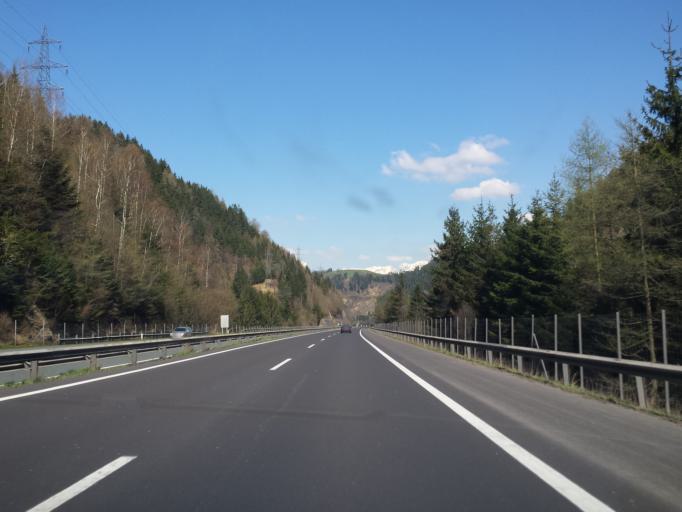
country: AT
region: Styria
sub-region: Politischer Bezirk Leoben
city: Sankt Michael in Obersteiermark
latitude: 47.3059
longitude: 15.0610
